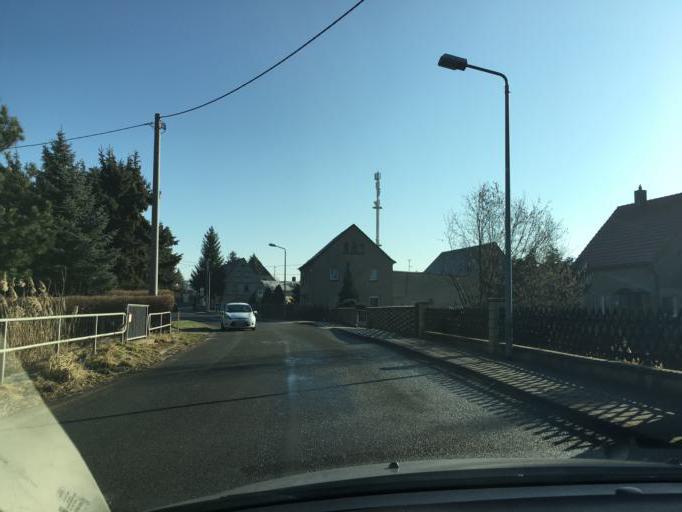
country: DE
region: Saxony
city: Belgershain
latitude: 51.2377
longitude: 12.5505
